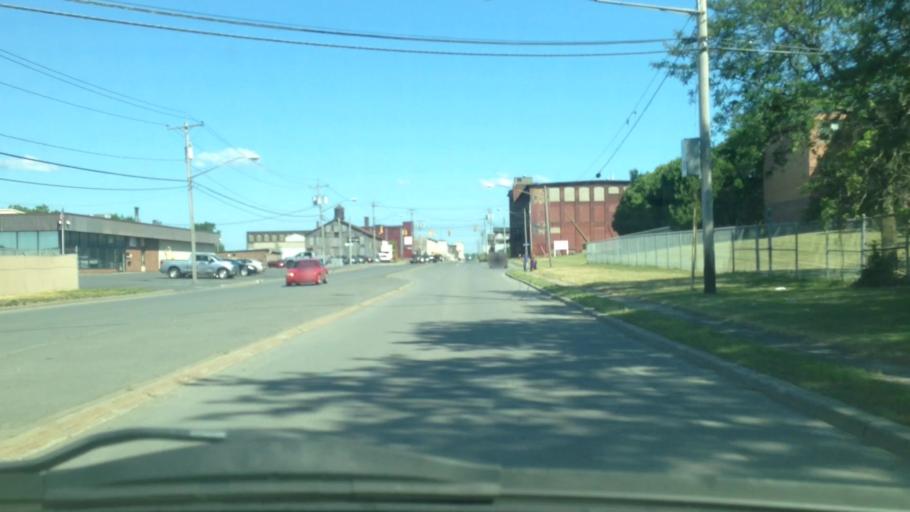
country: US
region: New York
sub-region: Oneida County
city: Utica
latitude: 43.1012
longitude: -75.2184
